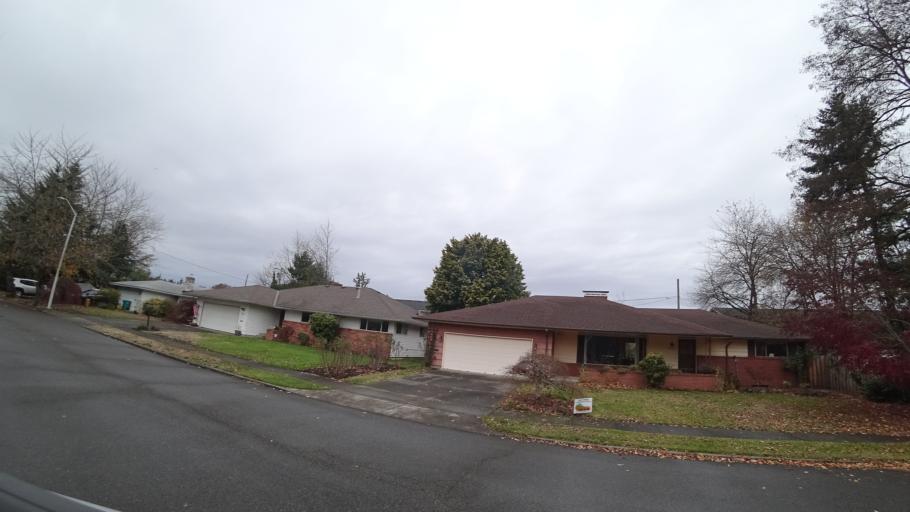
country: US
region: Oregon
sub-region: Multnomah County
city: Lents
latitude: 45.5321
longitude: -122.5525
